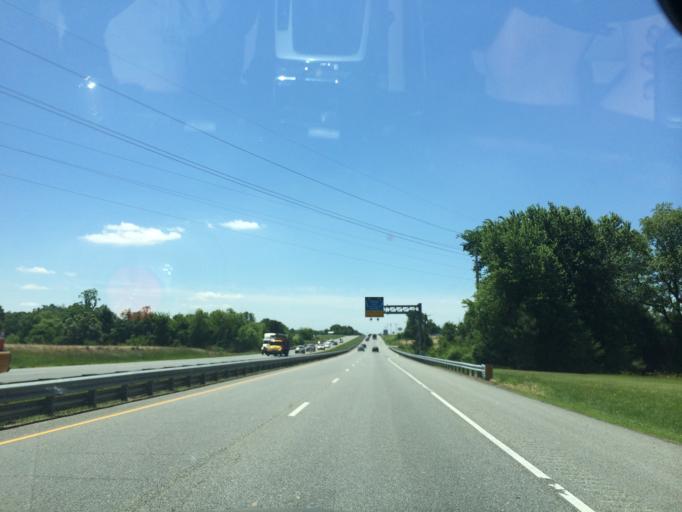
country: US
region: Maryland
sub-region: Talbot County
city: Easton
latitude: 38.8398
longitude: -76.0606
